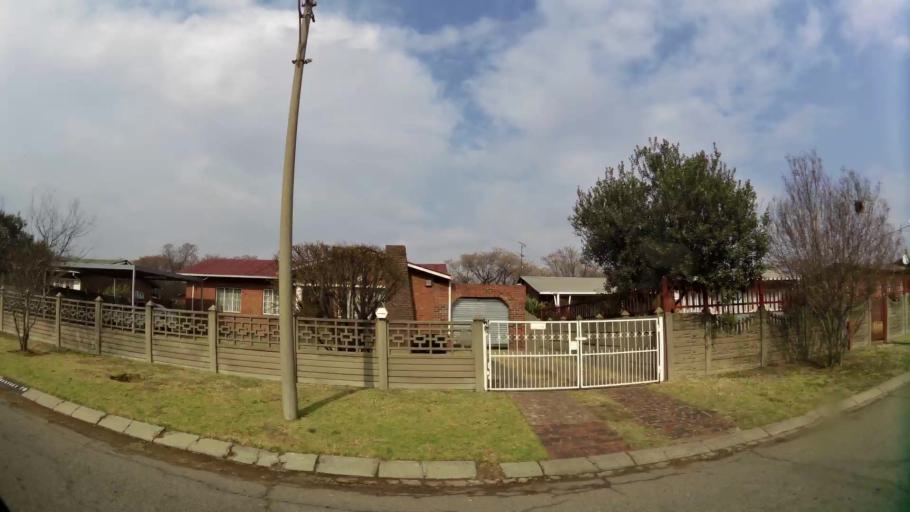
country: ZA
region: Gauteng
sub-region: Sedibeng District Municipality
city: Vanderbijlpark
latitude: -26.6875
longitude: 27.8382
